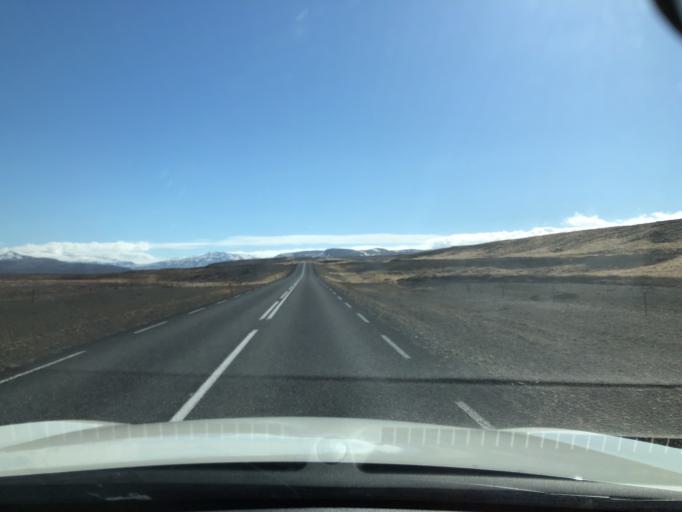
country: IS
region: South
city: Hveragerdi
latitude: 64.6996
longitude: -21.0760
